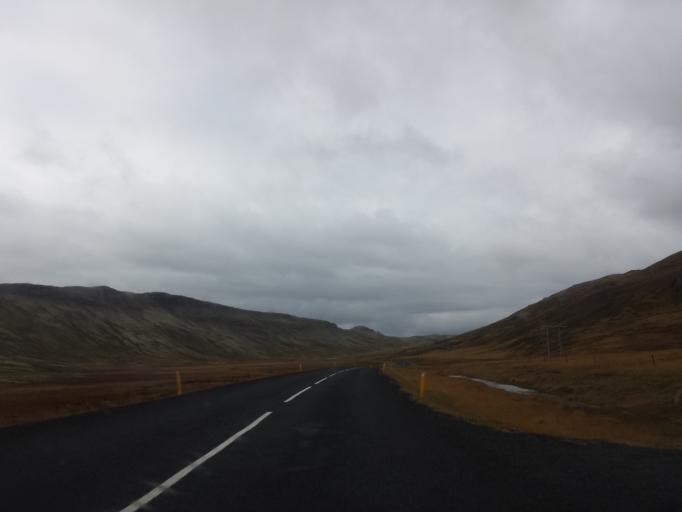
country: IS
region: West
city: Stykkisholmur
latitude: 64.8867
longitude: -22.8180
